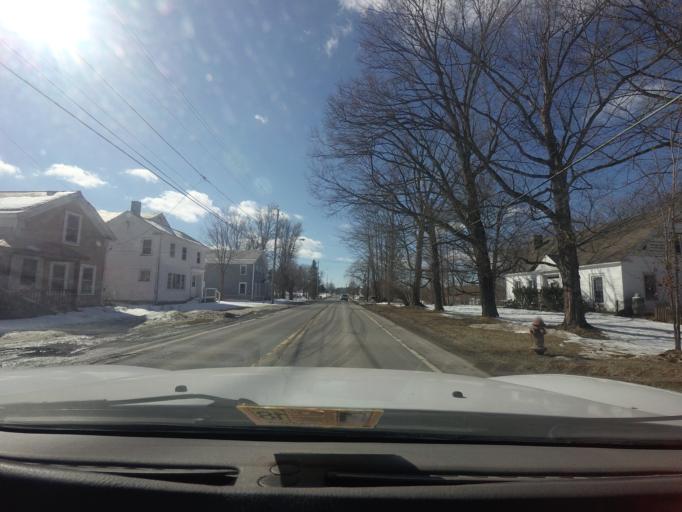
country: US
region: New York
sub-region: Washington County
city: Cambridge
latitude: 43.1626
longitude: -73.3327
